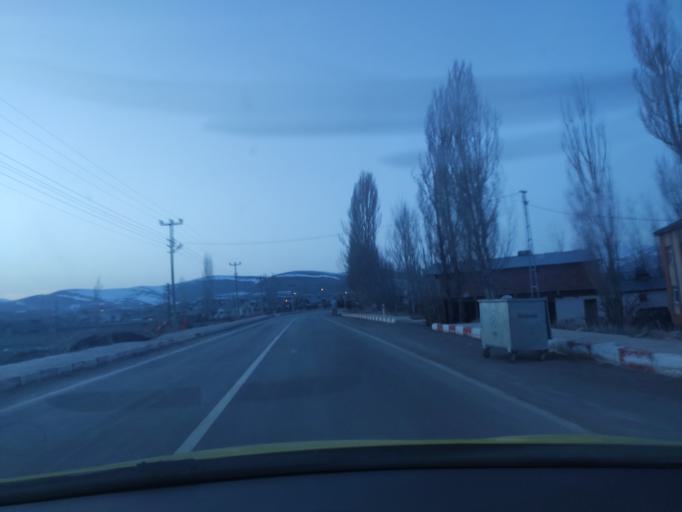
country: TR
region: Bayburt
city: Aydintepe
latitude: 40.3524
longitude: 40.1056
